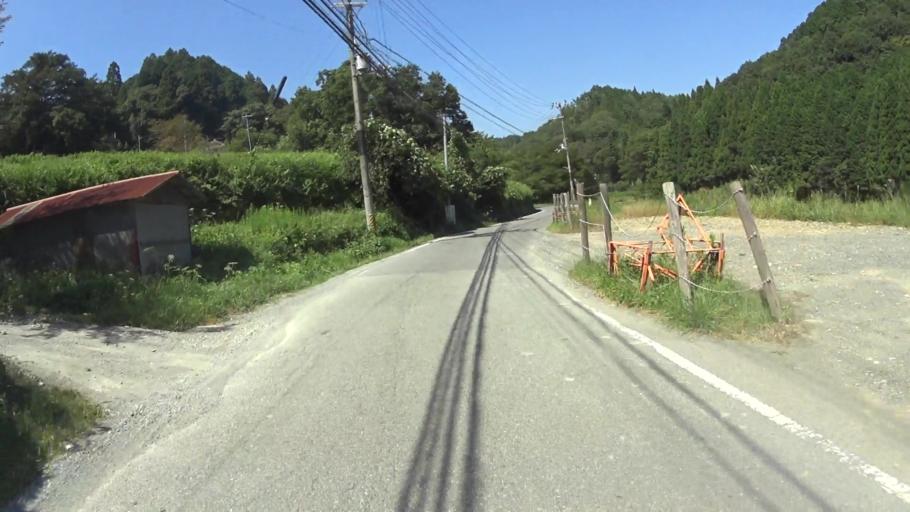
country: JP
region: Kyoto
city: Kameoka
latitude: 34.9408
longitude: 135.5357
